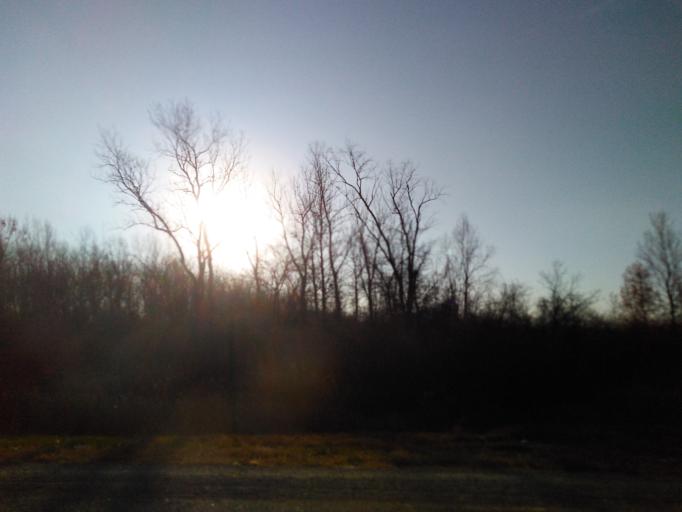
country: US
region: Illinois
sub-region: Saint Clair County
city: Alorton
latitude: 38.5861
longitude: -90.1019
